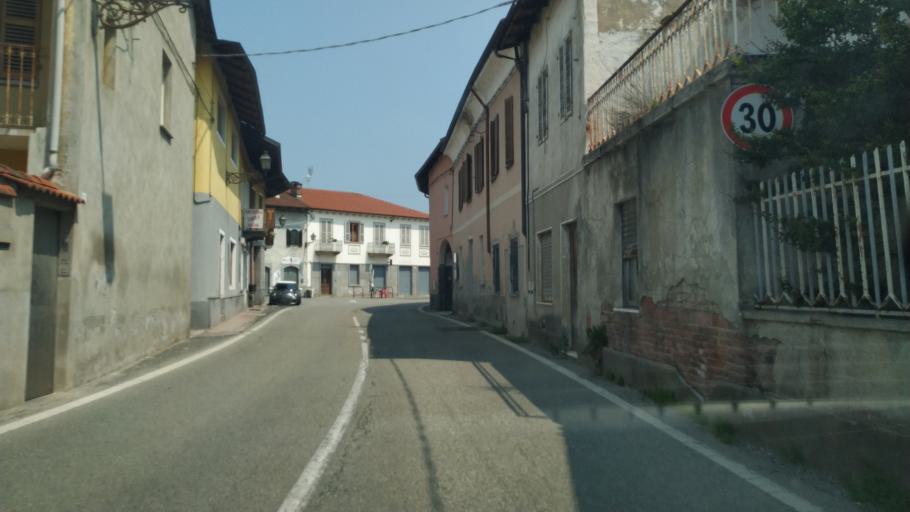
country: IT
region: Piedmont
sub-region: Provincia di Torino
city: Rondissone
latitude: 45.2456
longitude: 7.9636
